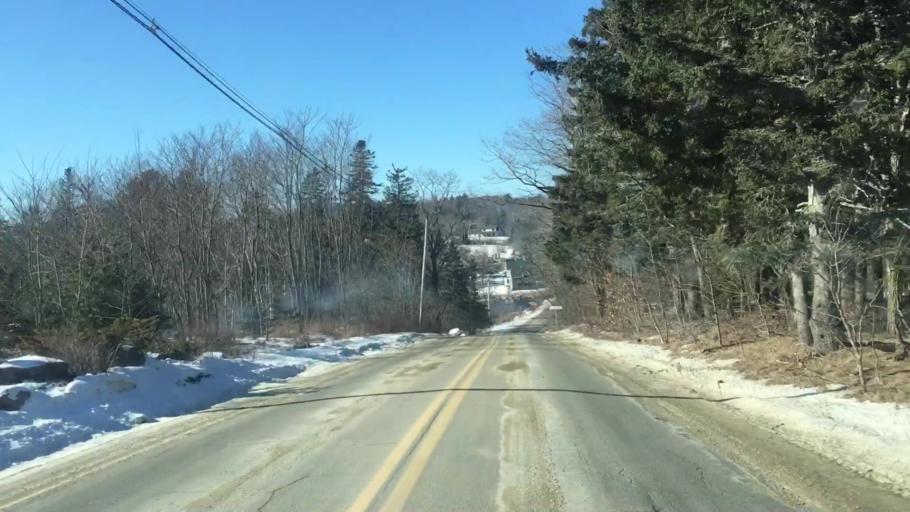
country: US
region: Maine
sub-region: Hancock County
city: Sedgwick
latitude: 44.3449
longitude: -68.6803
